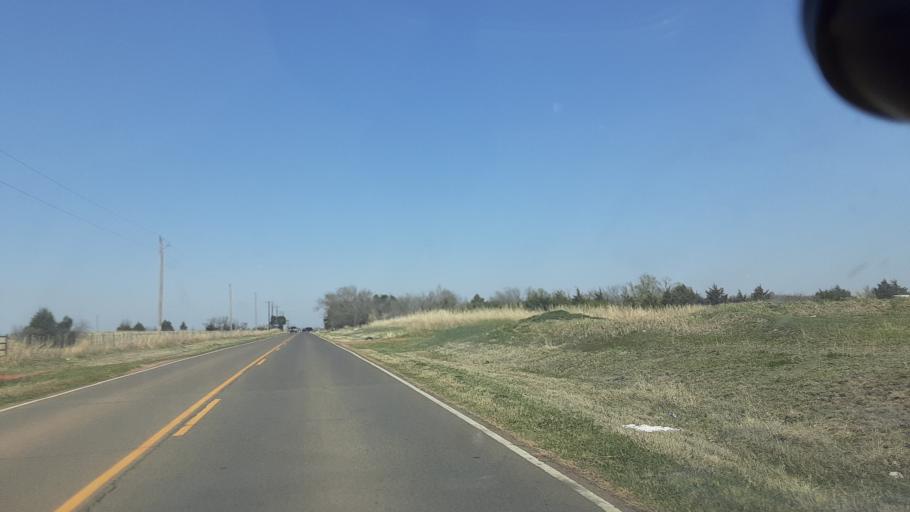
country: US
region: Oklahoma
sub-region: Logan County
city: Guthrie
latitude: 35.7800
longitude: -97.4784
